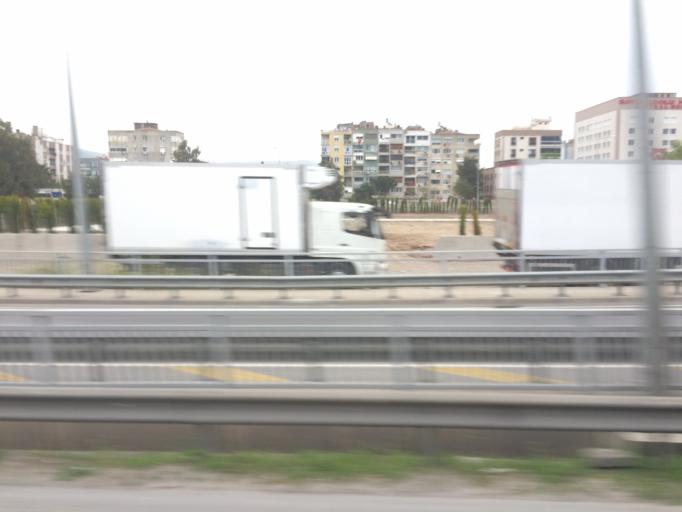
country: TR
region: Izmir
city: Karsiyaka
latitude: 38.4609
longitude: 27.1648
